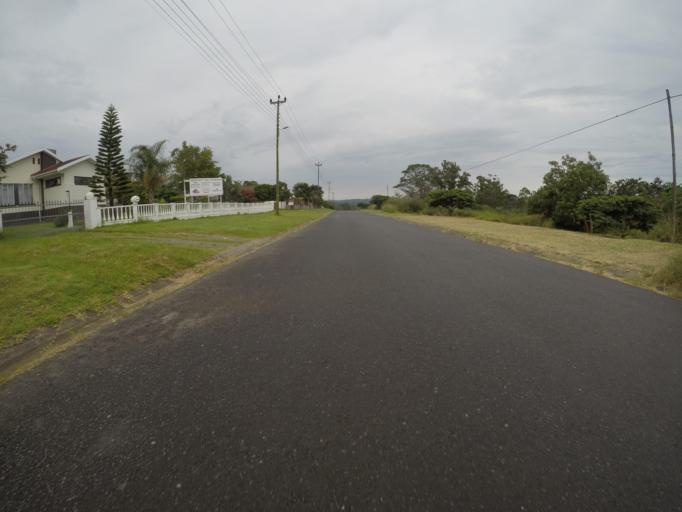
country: ZA
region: Eastern Cape
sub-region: Buffalo City Metropolitan Municipality
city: East London
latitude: -32.9628
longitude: 27.8396
